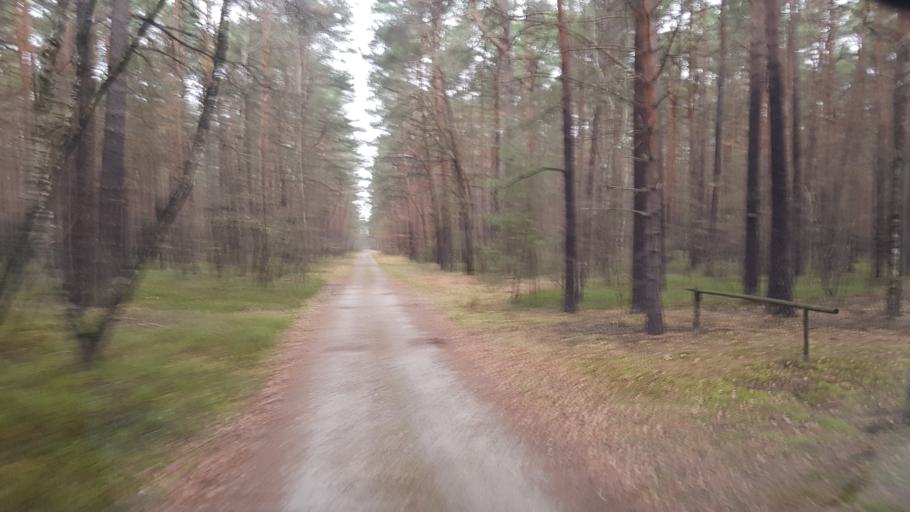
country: DE
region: Brandenburg
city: Finsterwalde
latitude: 51.6131
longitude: 13.7781
